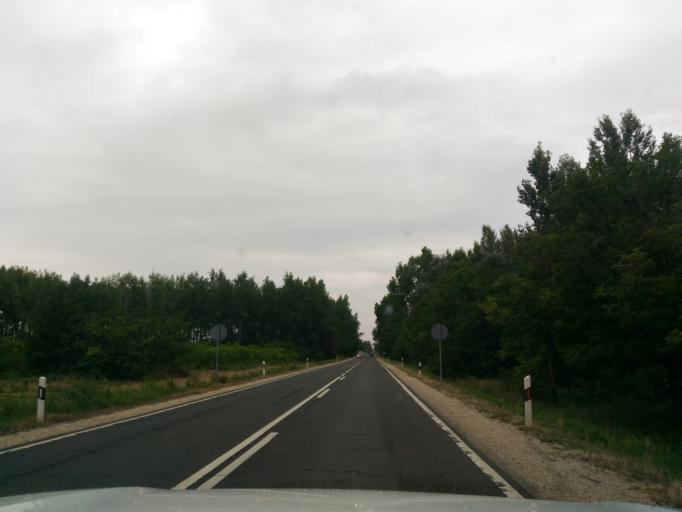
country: HU
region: Pest
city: Alsonemedi
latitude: 47.2964
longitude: 19.1837
